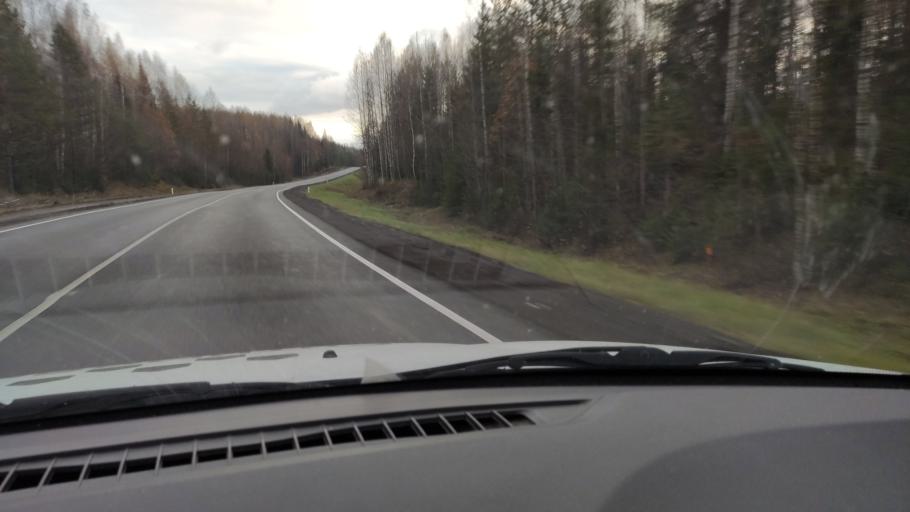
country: RU
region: Kirov
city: Omutninsk
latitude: 58.7495
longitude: 52.0589
